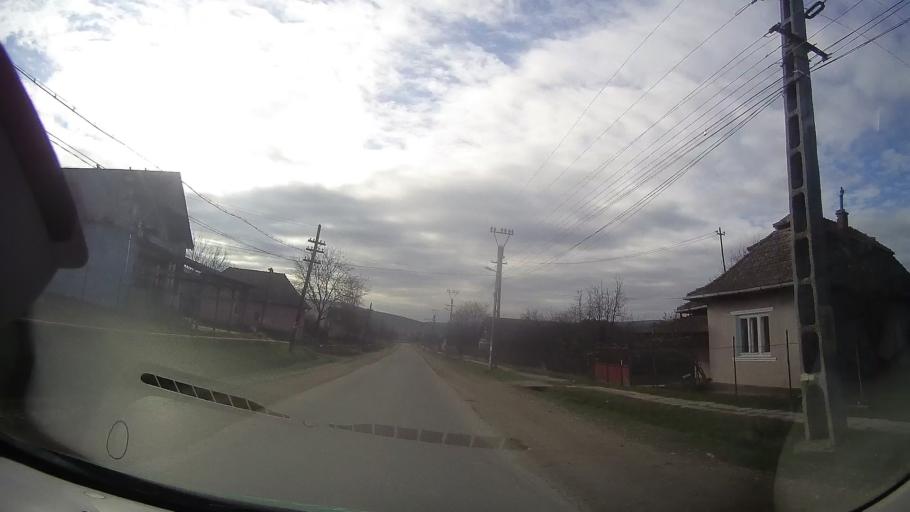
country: RO
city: Barza
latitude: 46.5538
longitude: 24.1308
